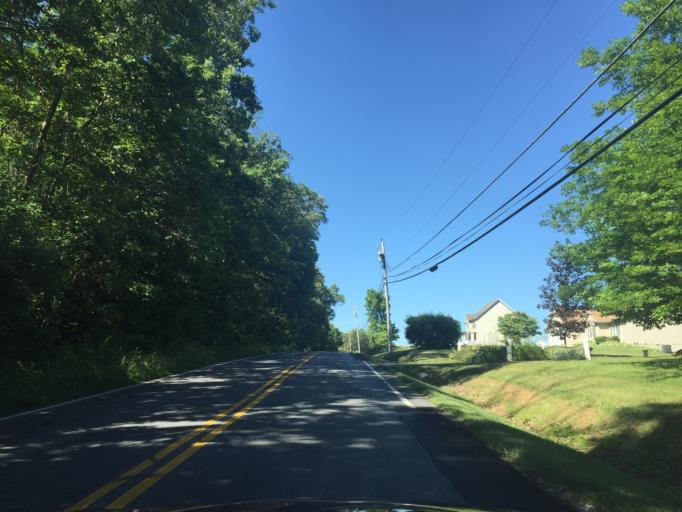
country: US
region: Maryland
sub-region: Carroll County
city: Westminster
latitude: 39.5832
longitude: -76.9327
